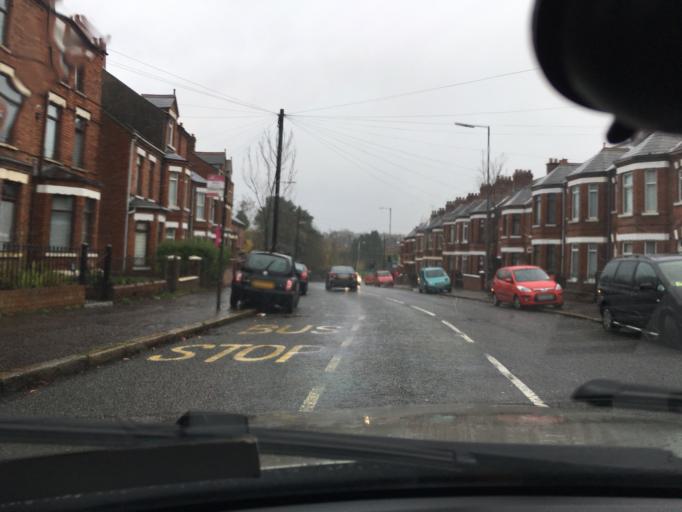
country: GB
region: Northern Ireland
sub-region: City of Belfast
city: Belfast
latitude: 54.6086
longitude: -5.9730
